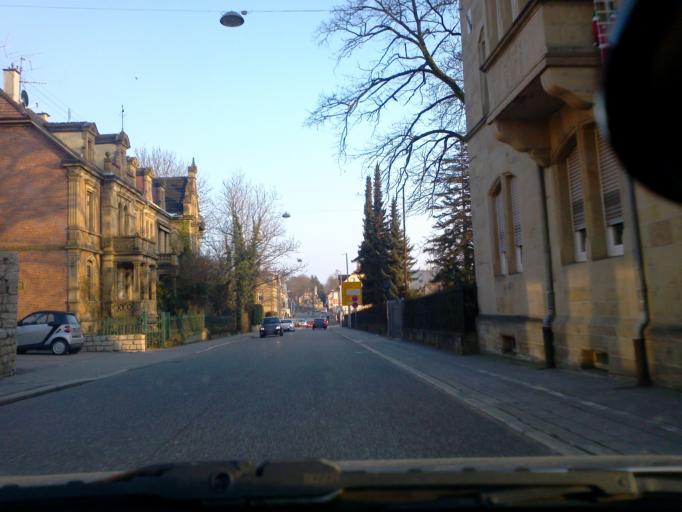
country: DE
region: Baden-Wuerttemberg
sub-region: Karlsruhe Region
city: Bretten
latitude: 49.0348
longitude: 8.7145
